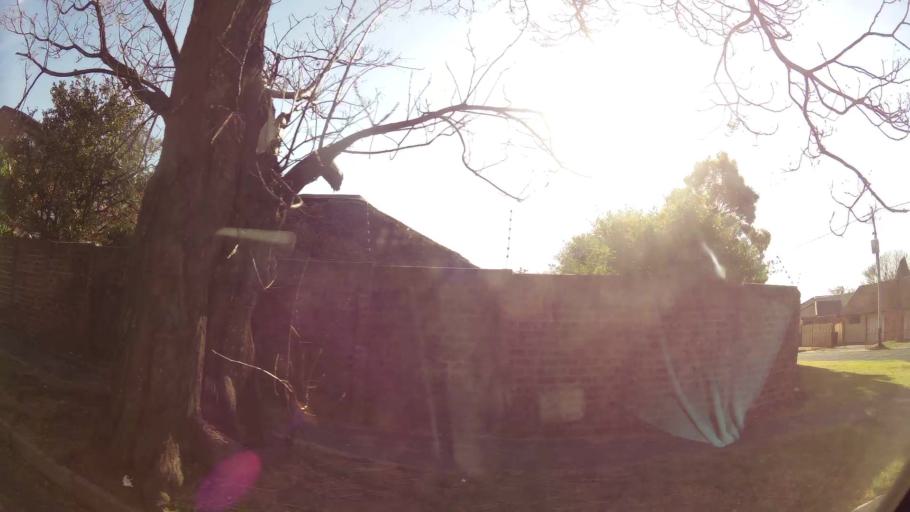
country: ZA
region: Gauteng
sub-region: City of Johannesburg Metropolitan Municipality
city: Johannesburg
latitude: -26.2525
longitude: 28.0123
